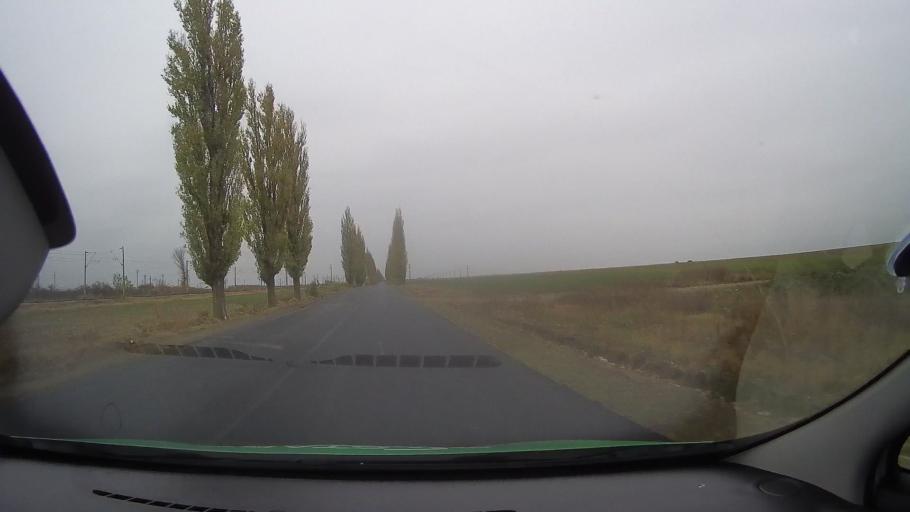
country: RO
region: Ialomita
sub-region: Comuna Valea Ciorii
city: Valea Ciorii
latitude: 44.7111
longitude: 27.5921
